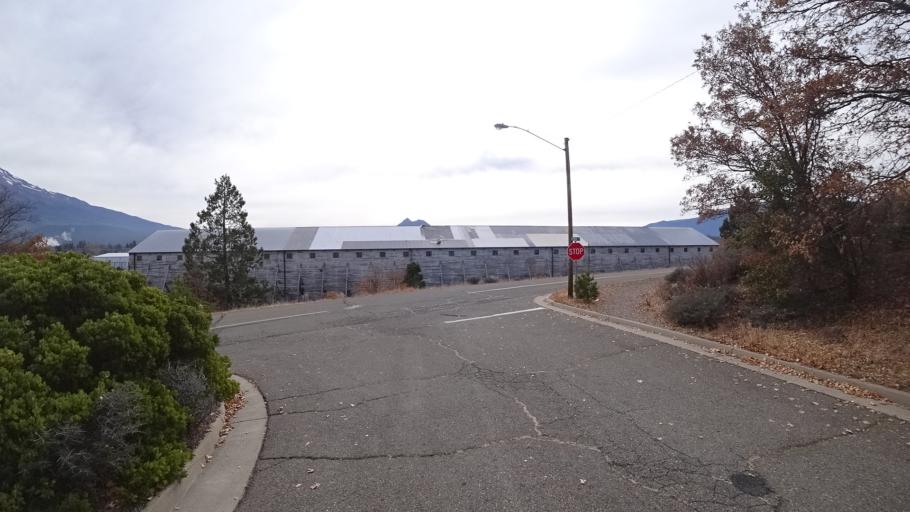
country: US
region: California
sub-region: Siskiyou County
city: Weed
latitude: 41.4338
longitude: -122.3856
